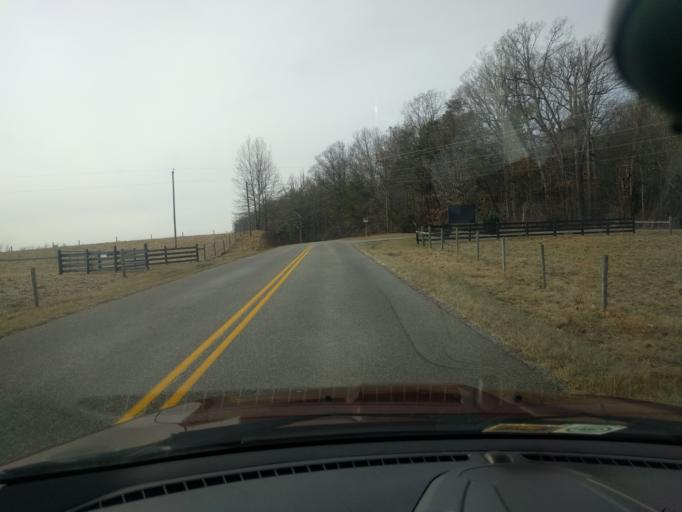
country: US
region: Virginia
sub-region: Augusta County
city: Stuarts Draft
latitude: 37.9311
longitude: -79.2175
